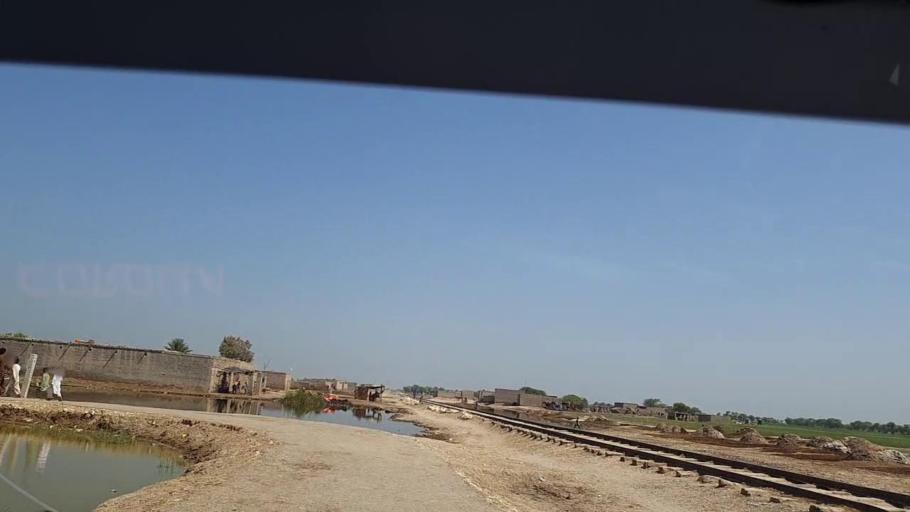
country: PK
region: Sindh
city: Tangwani
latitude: 28.2811
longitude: 69.0384
